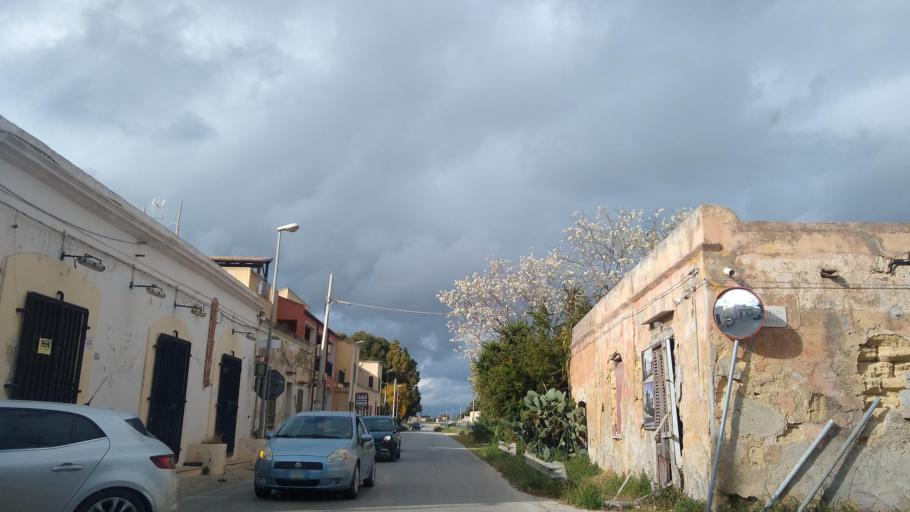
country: IT
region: Sicily
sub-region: Trapani
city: Marsala
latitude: 37.8556
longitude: 12.4870
